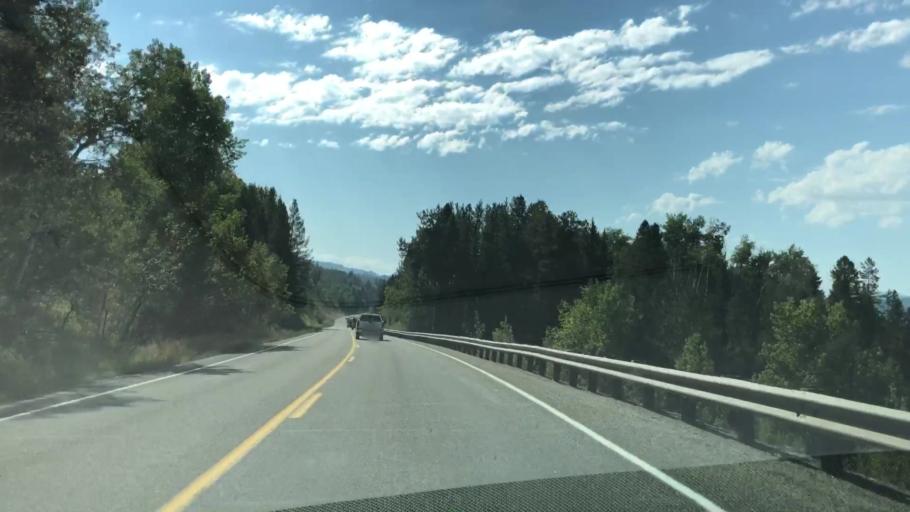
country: US
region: Idaho
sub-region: Teton County
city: Victor
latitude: 43.2970
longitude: -111.1286
